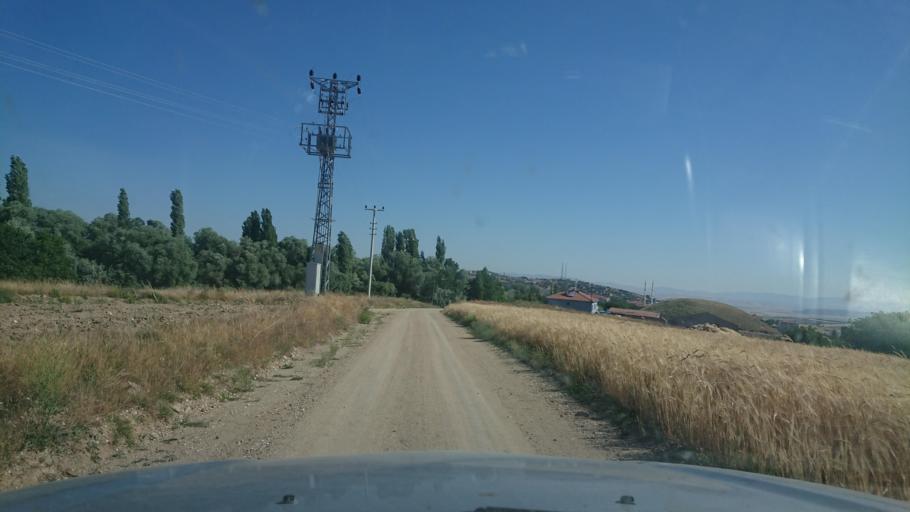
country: TR
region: Aksaray
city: Agacoren
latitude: 38.8605
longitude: 33.9122
